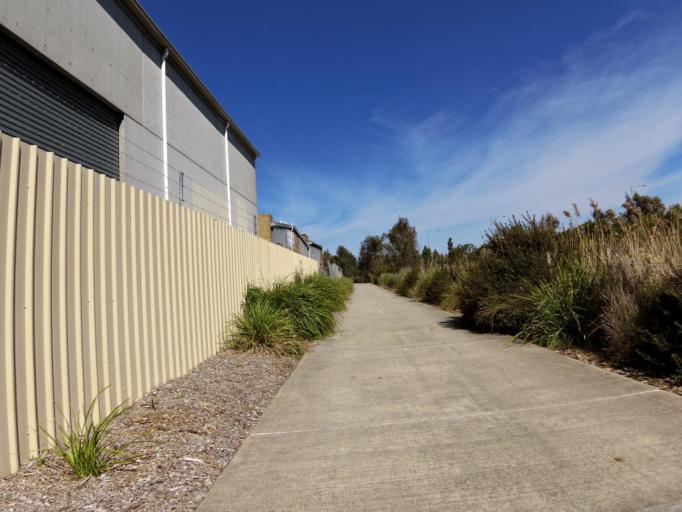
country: AU
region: Victoria
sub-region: Greater Dandenong
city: Dandenong
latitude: -37.9882
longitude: 145.1941
